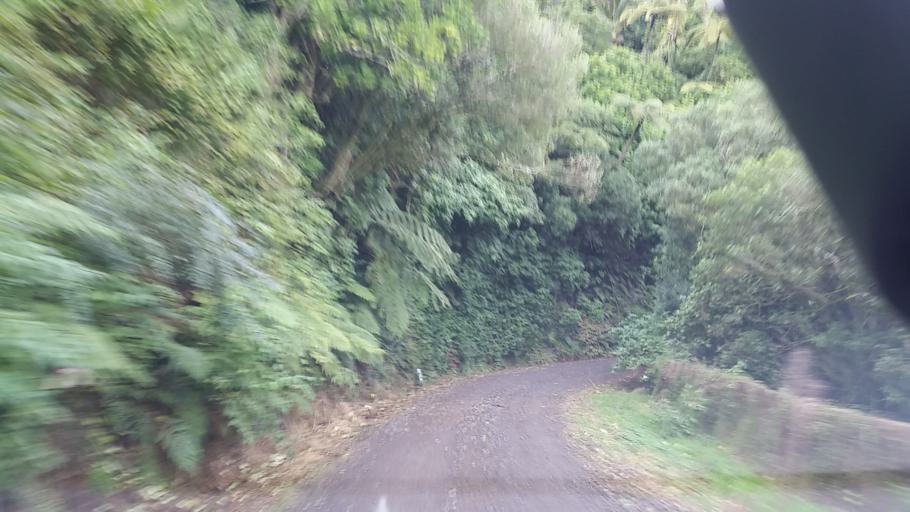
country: NZ
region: Taranaki
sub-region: New Plymouth District
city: Waitara
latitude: -39.0690
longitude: 174.3937
